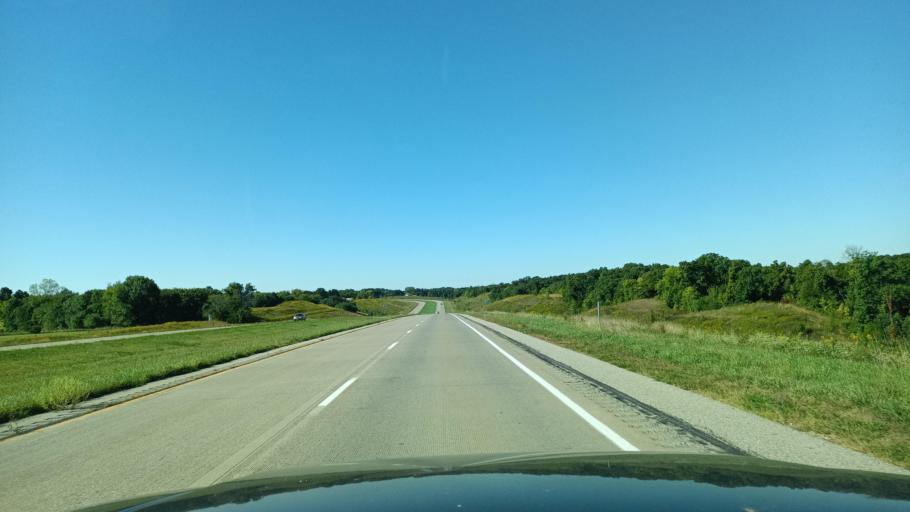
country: US
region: Iowa
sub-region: Lee County
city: Fort Madison
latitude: 40.6496
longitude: -91.3669
